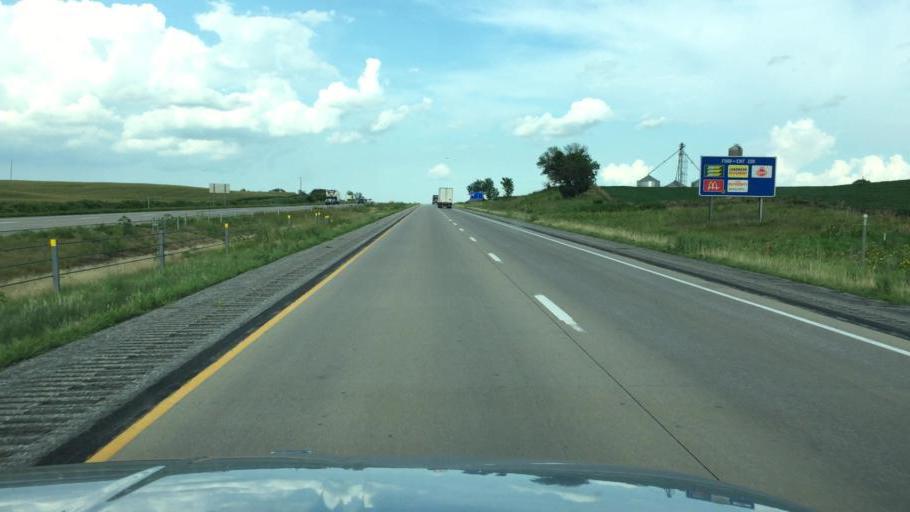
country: US
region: Iowa
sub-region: Iowa County
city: Williamsburg
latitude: 41.6871
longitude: -92.0414
